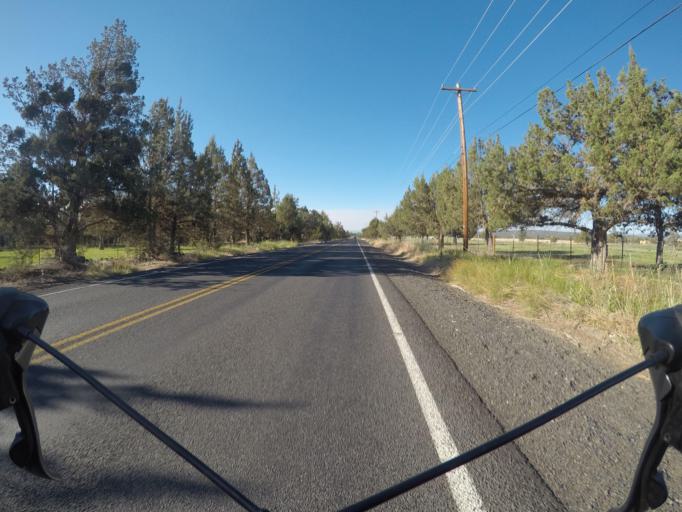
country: US
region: Oregon
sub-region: Deschutes County
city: Redmond
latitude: 44.2077
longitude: -121.2436
